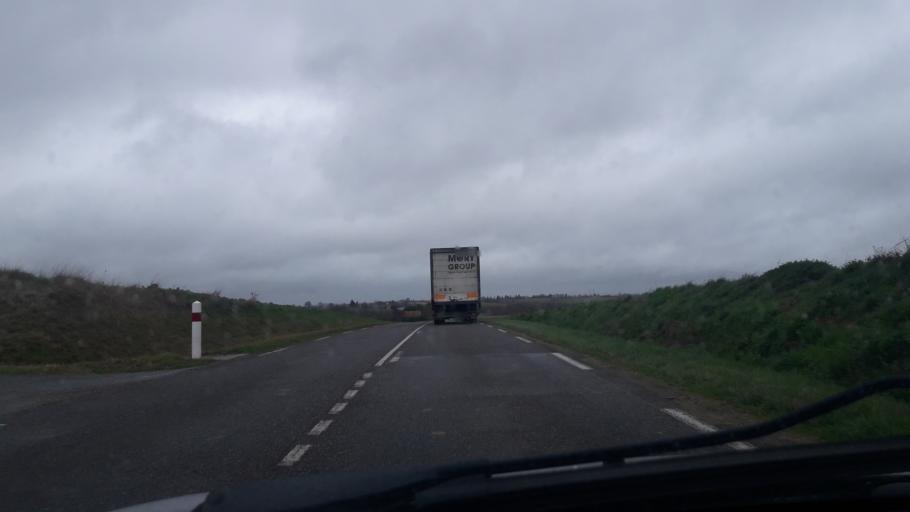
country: FR
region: Midi-Pyrenees
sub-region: Departement du Gers
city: Gimont
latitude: 43.7034
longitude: 0.9946
